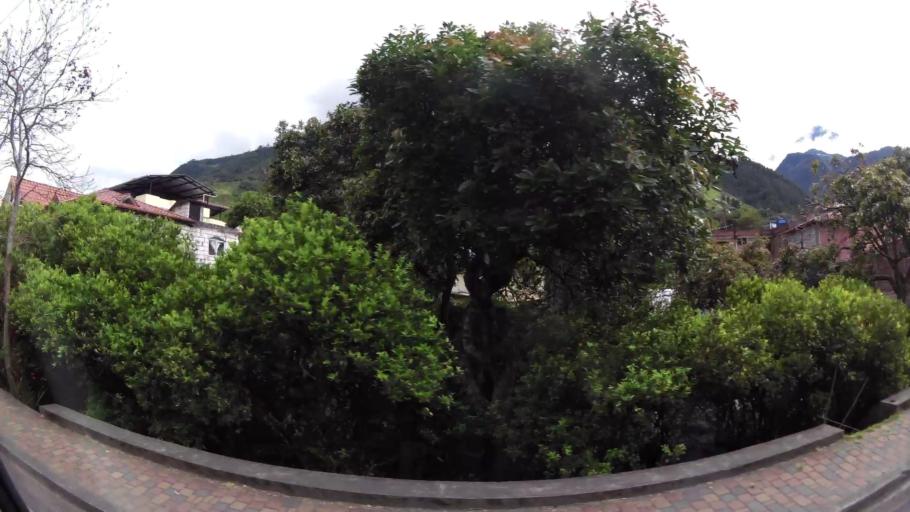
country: EC
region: Tungurahua
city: Banos
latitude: -1.3944
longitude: -78.3963
